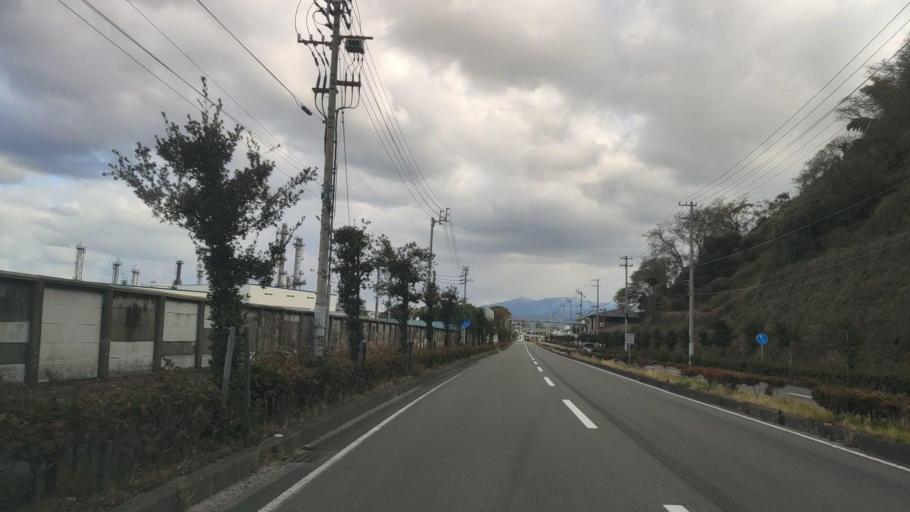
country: JP
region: Ehime
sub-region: Shikoku-chuo Shi
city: Matsuyama
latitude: 33.8452
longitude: 132.7092
